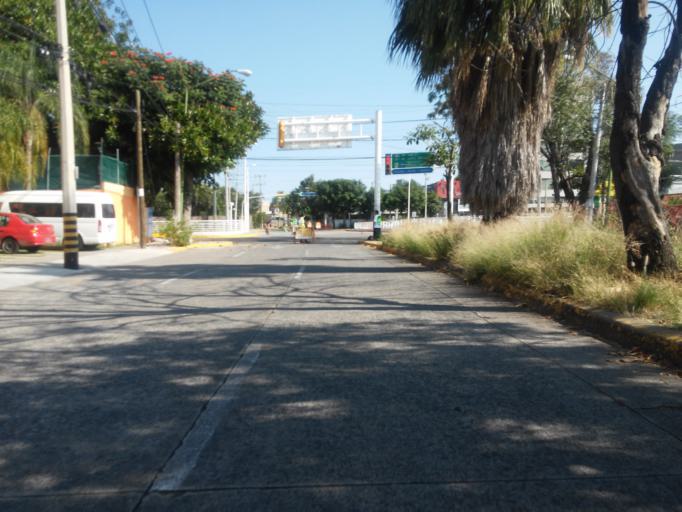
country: MX
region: Jalisco
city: Guadalajara
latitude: 20.6609
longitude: -103.3880
